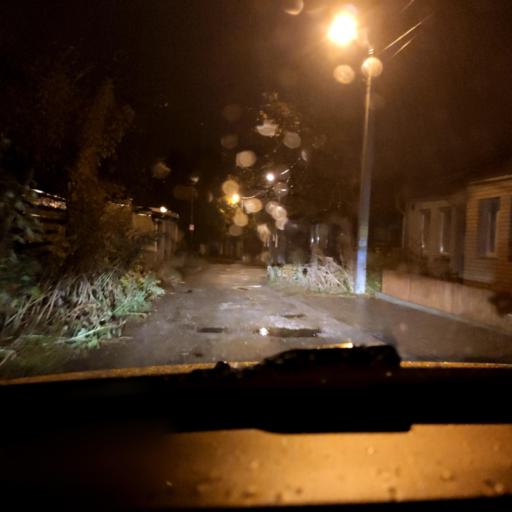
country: RU
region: Voronezj
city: Voronezh
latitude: 51.6336
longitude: 39.1961
